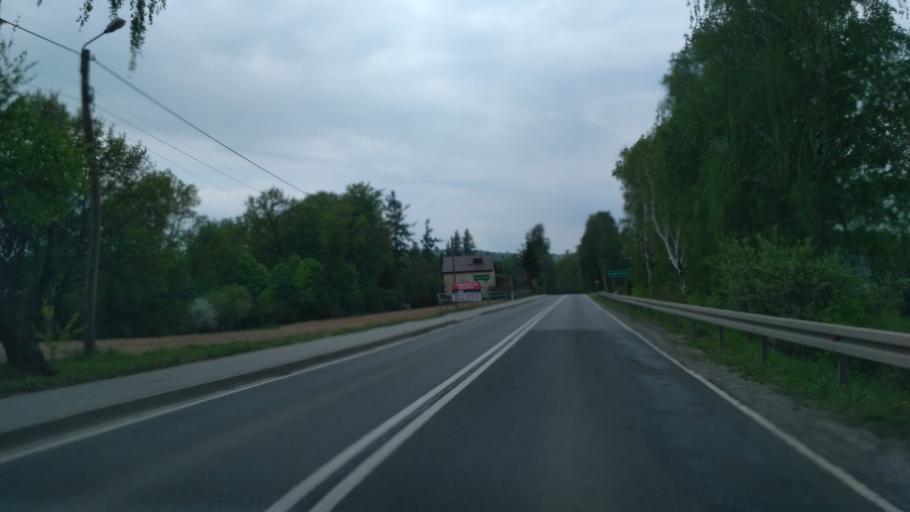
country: PL
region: Lesser Poland Voivodeship
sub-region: Powiat tarnowski
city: Tarnowiec
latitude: 49.9642
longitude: 20.9931
